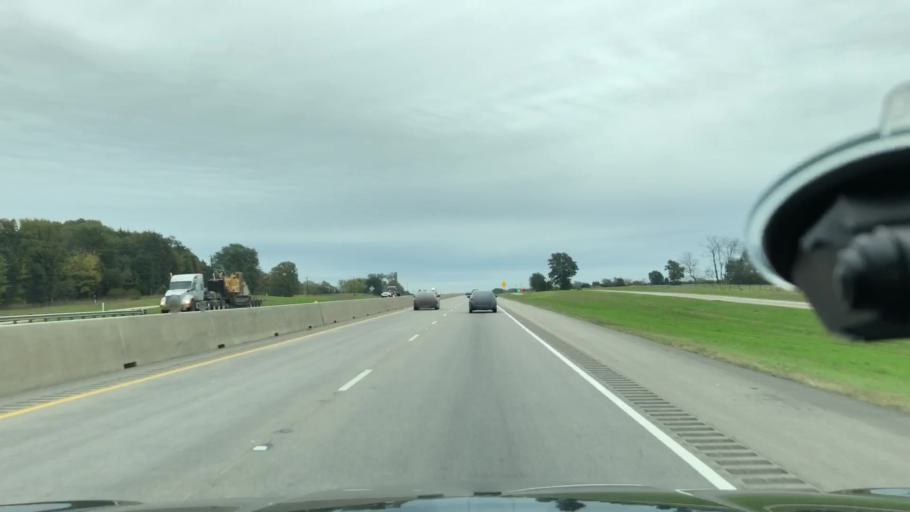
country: US
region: Texas
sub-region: Franklin County
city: Mount Vernon
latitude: 33.1642
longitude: -95.2731
